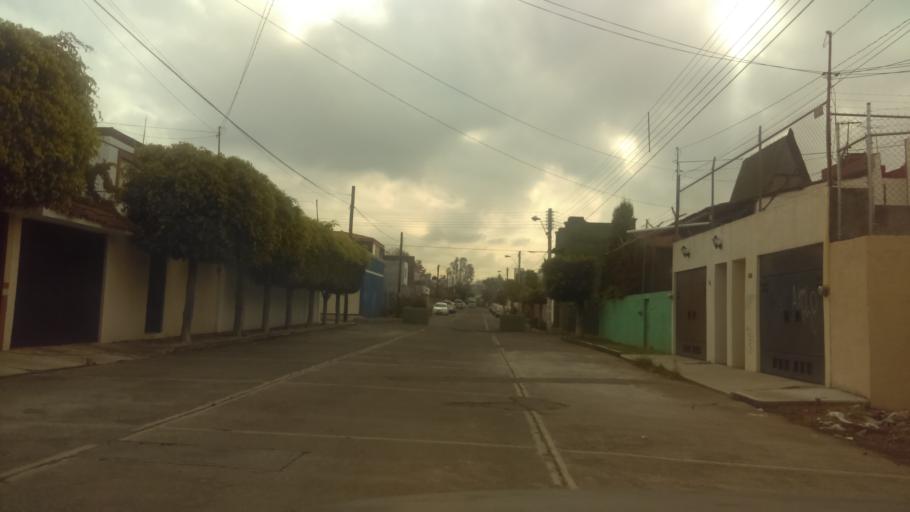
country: MX
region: Michoacan
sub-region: Morelia
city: Montana Monarca (Punta Altozano)
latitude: 19.6730
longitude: -101.1863
